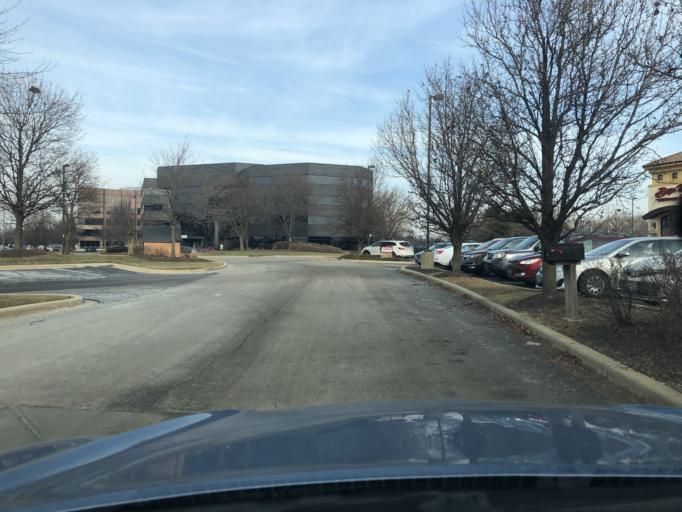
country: US
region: Illinois
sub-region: DuPage County
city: Itasca
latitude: 41.9874
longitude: -88.0045
